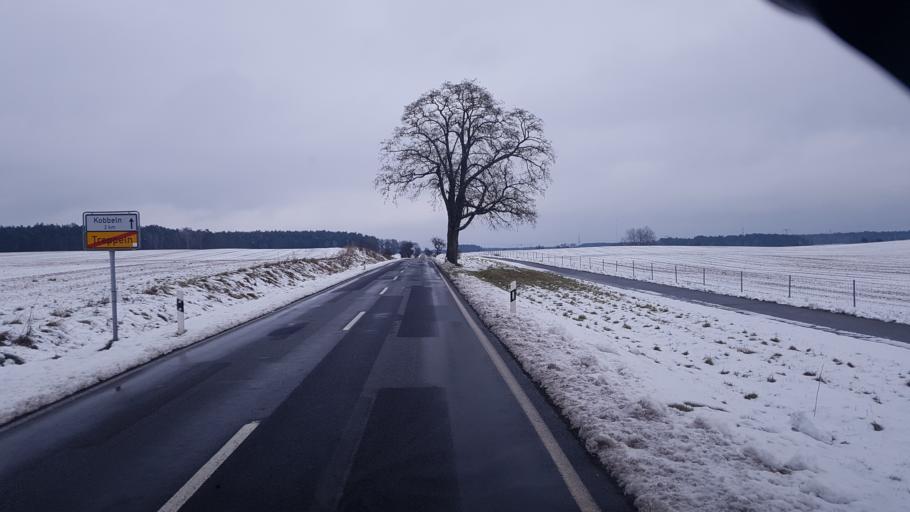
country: DE
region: Brandenburg
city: Lawitz
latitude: 52.0820
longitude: 14.5467
